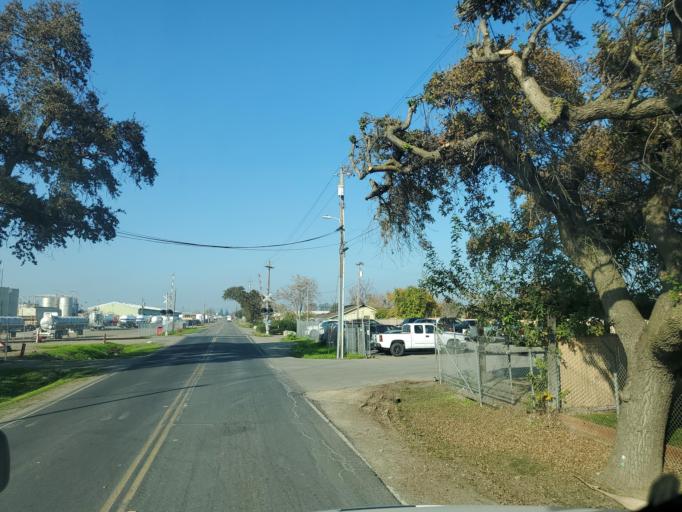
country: US
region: California
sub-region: San Joaquin County
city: August
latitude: 37.9744
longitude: -121.2496
